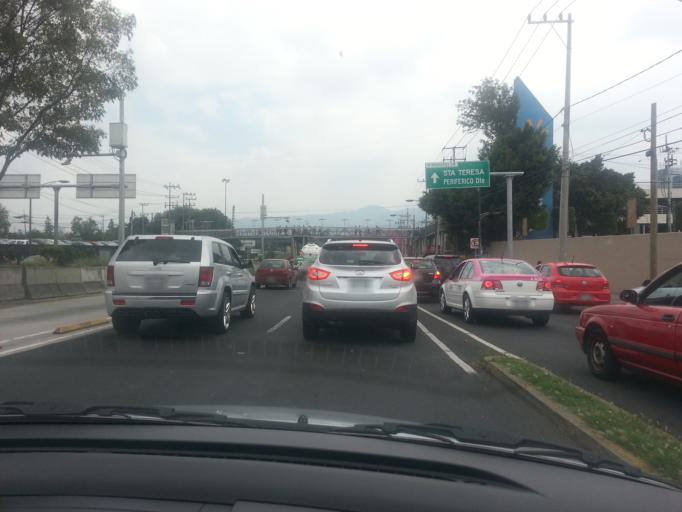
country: MX
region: Mexico City
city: Tlalpan
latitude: 19.3061
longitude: -99.1865
